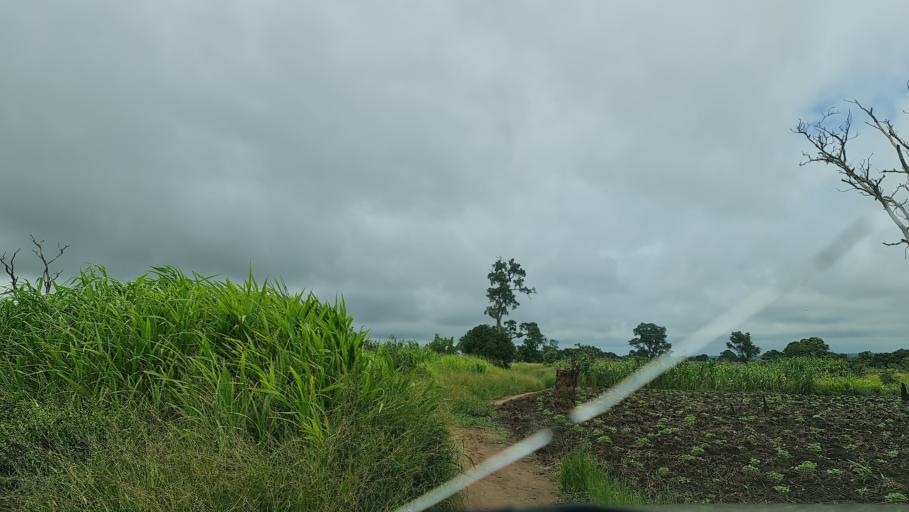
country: MW
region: Southern Region
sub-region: Nsanje District
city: Nsanje
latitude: -17.3396
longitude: 35.7205
